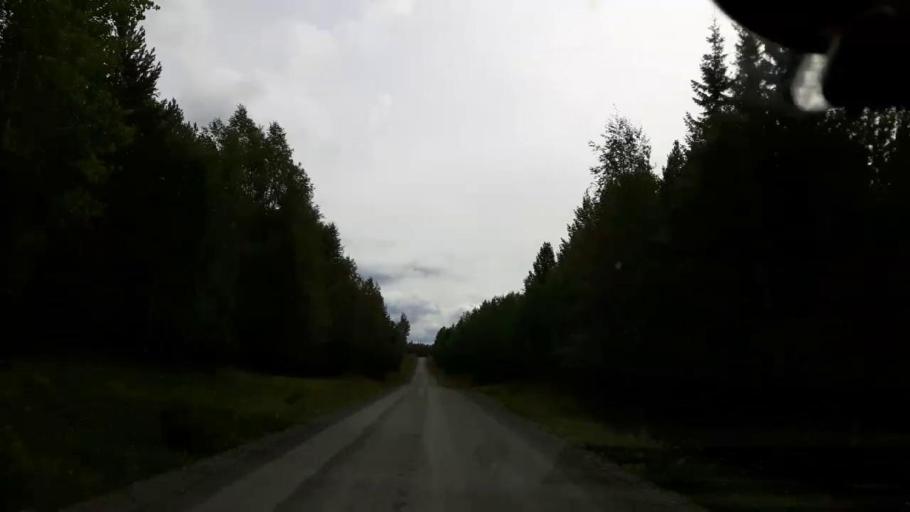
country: SE
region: Jaemtland
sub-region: Krokoms Kommun
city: Valla
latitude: 63.6554
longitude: 13.9784
